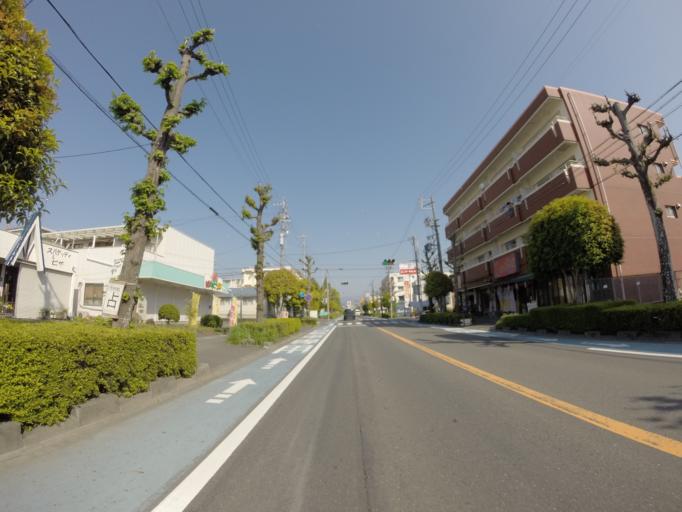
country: JP
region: Shizuoka
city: Shizuoka-shi
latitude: 34.9452
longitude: 138.3743
